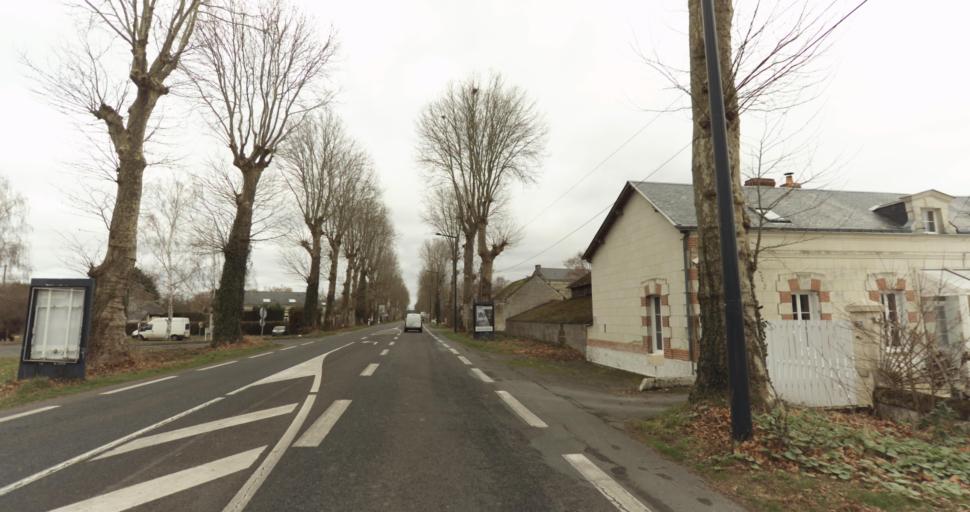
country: FR
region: Pays de la Loire
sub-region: Departement de Maine-et-Loire
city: Saumur
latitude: 47.2824
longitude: -0.0524
